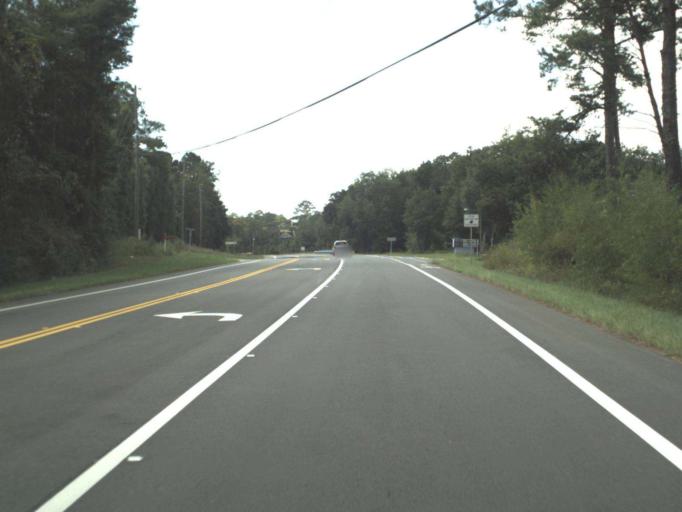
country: US
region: Florida
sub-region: Walton County
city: Freeport
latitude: 30.5118
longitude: -86.1931
